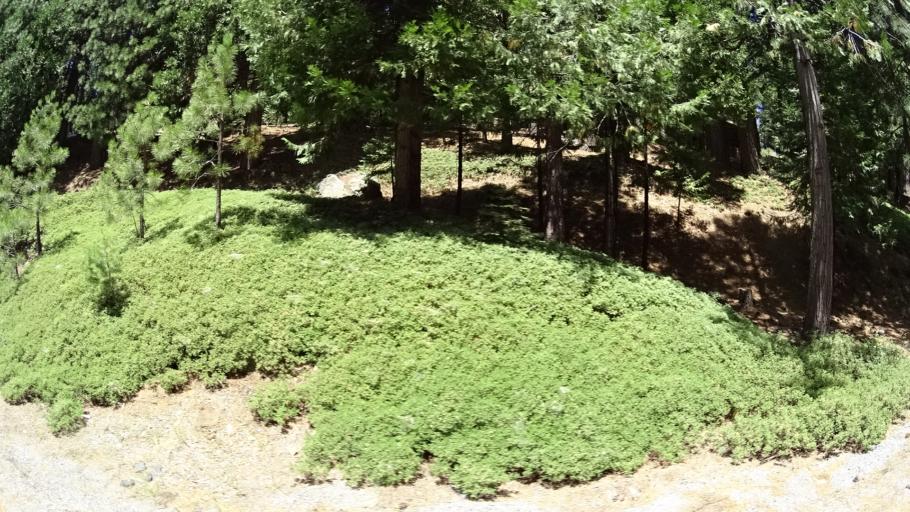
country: US
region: California
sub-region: Calaveras County
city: Arnold
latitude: 38.3006
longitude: -120.2569
